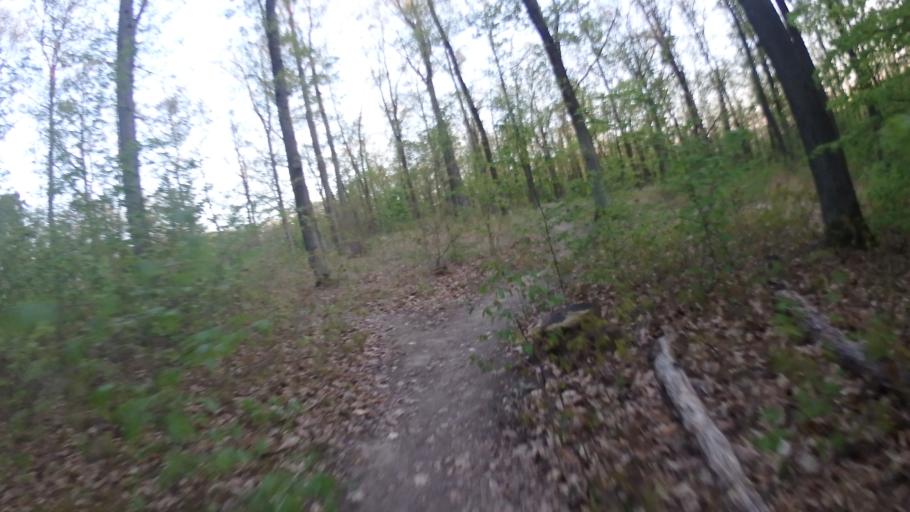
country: CZ
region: South Moravian
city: Troubsko
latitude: 49.1907
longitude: 16.5244
